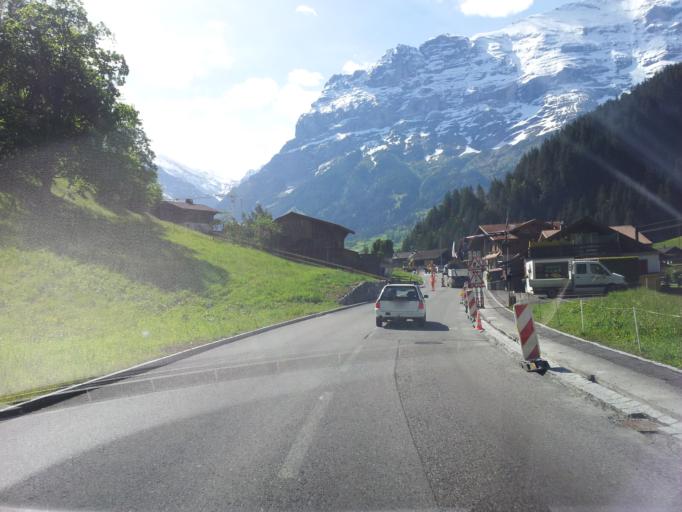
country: CH
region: Bern
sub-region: Interlaken-Oberhasli District
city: Grindelwald
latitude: 46.6322
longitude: 8.0023
